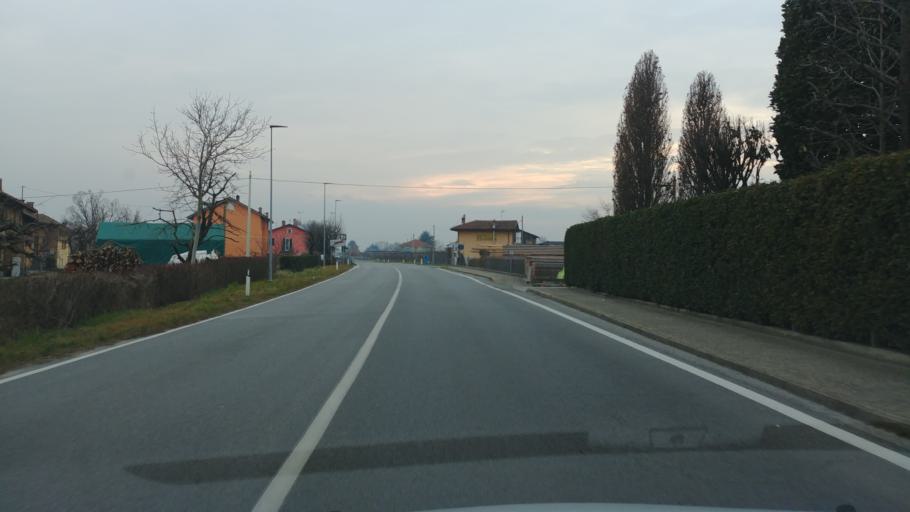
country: IT
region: Piedmont
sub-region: Provincia di Cuneo
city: Sant'Albano Stura
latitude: 44.5094
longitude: 7.6860
